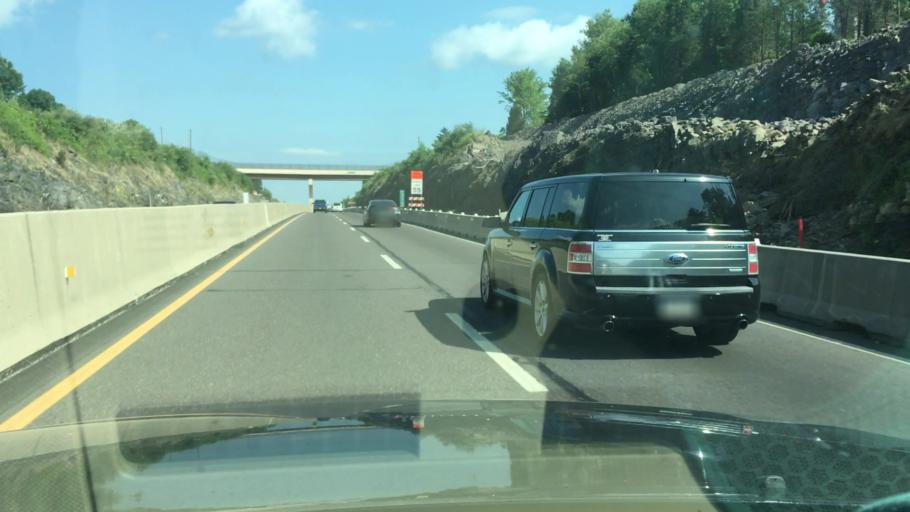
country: US
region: Pennsylvania
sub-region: Montgomery County
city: Telford
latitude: 40.3469
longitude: -75.3888
